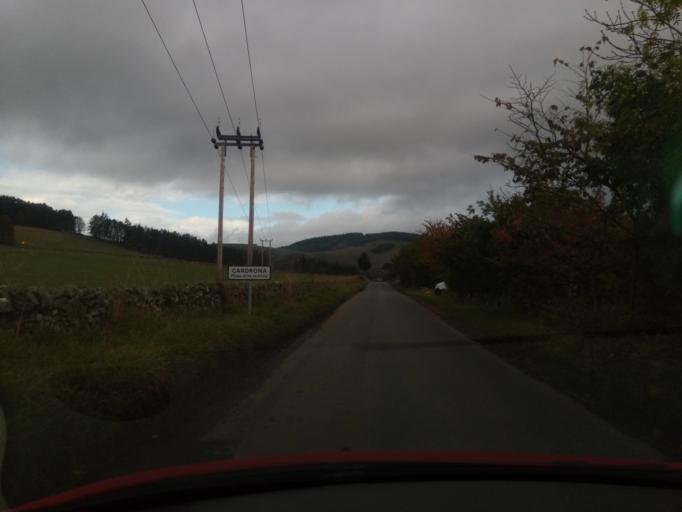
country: GB
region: Scotland
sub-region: The Scottish Borders
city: Innerleithen
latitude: 55.6337
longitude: -3.1057
